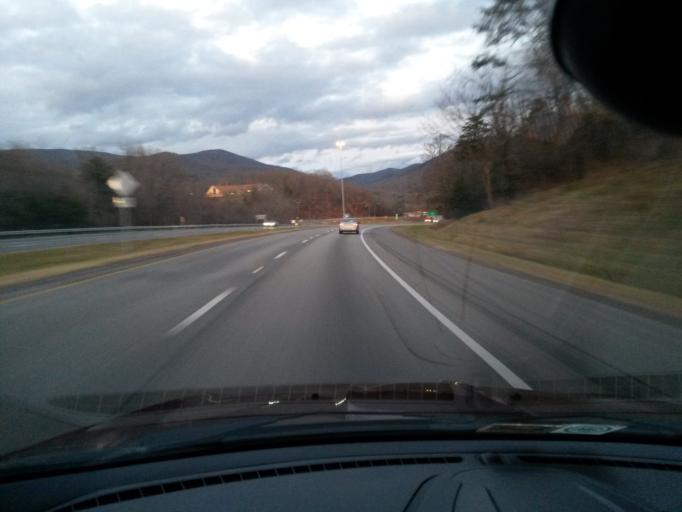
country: US
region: Virginia
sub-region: City of Covington
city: Fairlawn
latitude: 37.7755
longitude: -79.9779
